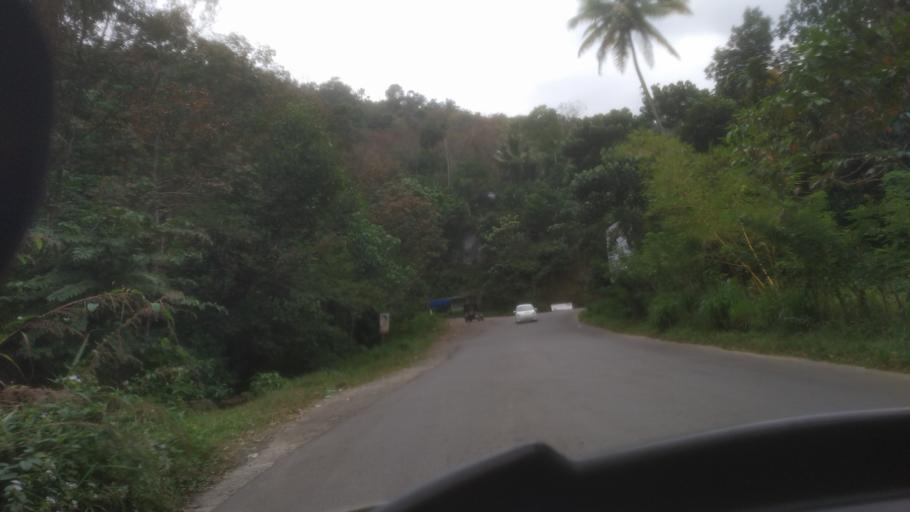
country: IN
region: Kerala
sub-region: Idukki
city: Idukki
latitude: 9.9736
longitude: 76.9996
